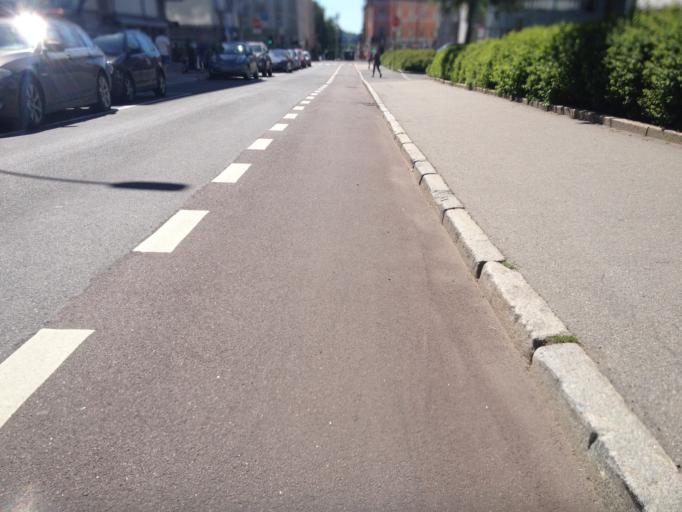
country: NO
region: Oslo
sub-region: Oslo
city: Oslo
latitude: 59.9293
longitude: 10.7587
